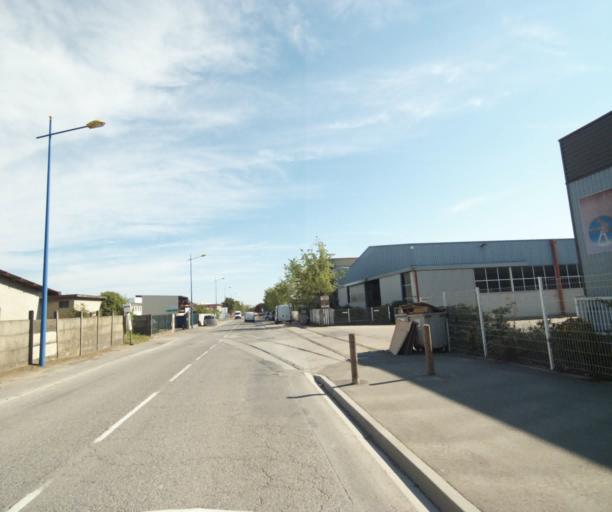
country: FR
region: Rhone-Alpes
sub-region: Departement de la Haute-Savoie
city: Marin
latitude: 46.3916
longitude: 6.5053
